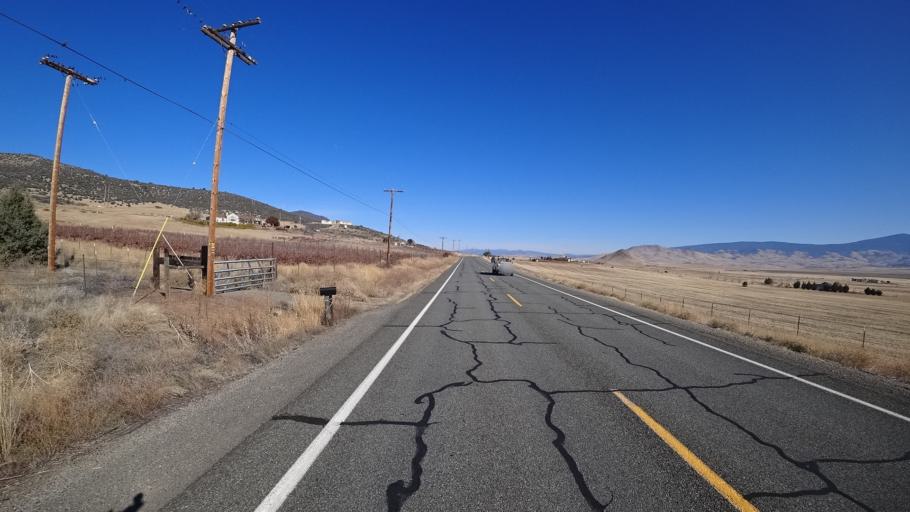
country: US
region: California
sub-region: Siskiyou County
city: Montague
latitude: 41.7956
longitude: -122.5115
